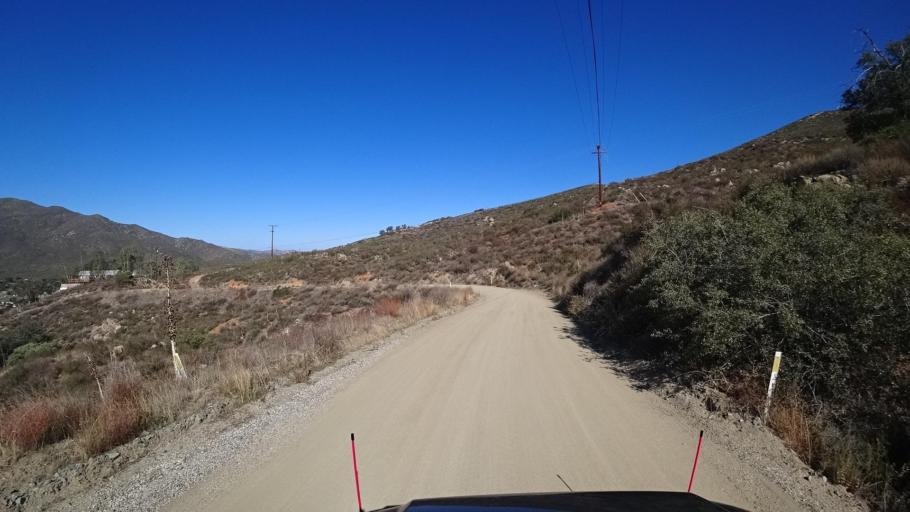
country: US
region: California
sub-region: San Diego County
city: Descanso
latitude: 32.8598
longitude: -116.6835
